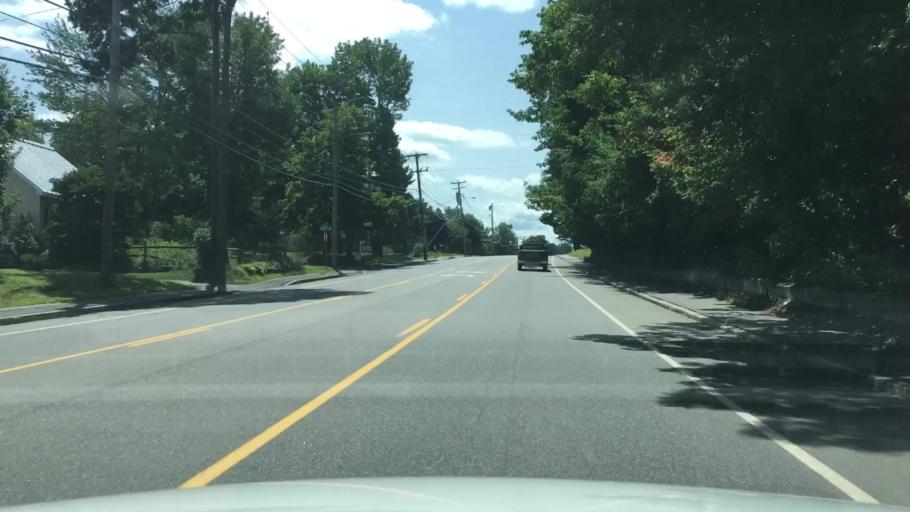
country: US
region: Maine
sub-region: Kennebec County
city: Augusta
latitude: 44.3060
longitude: -69.7654
